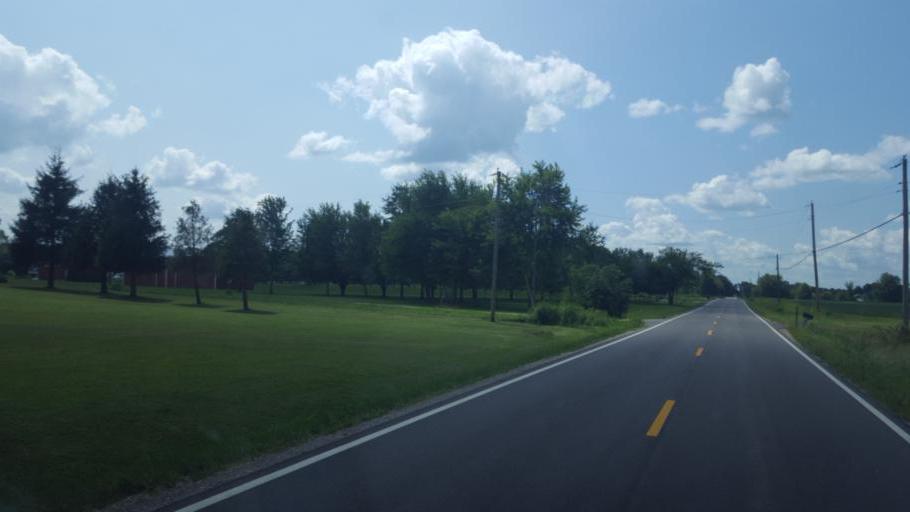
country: US
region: Ohio
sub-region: Delaware County
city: Ashley
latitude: 40.3371
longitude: -82.8920
